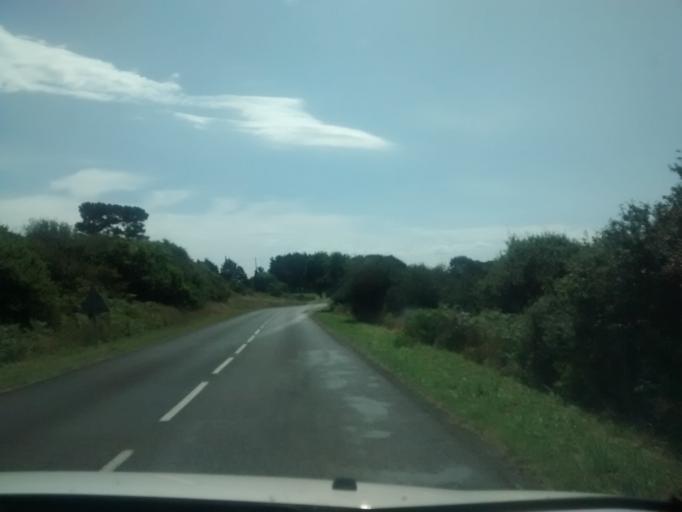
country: FR
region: Brittany
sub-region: Departement d'Ille-et-Vilaine
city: Cancale
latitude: 48.6968
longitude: -1.8604
